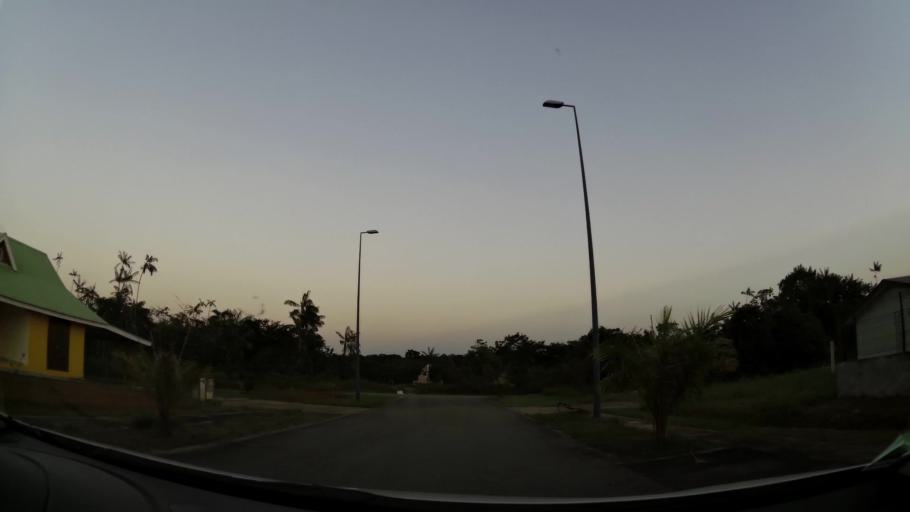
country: GF
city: Macouria
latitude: 4.9230
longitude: -52.4072
